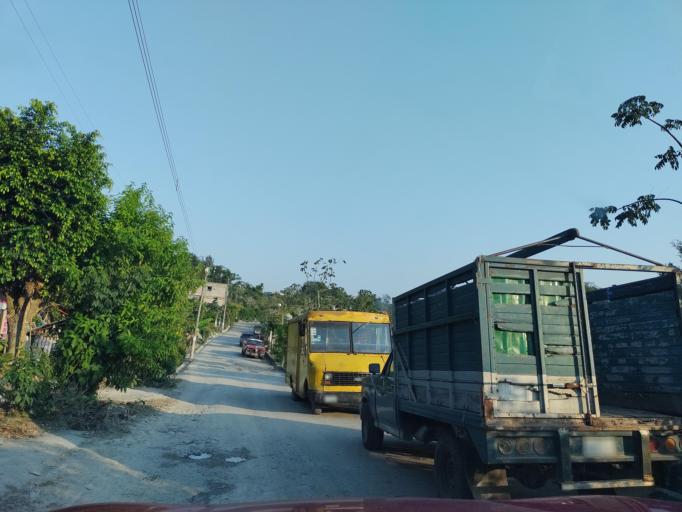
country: MX
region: Veracruz
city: Agua Dulce
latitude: 20.4057
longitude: -97.2912
